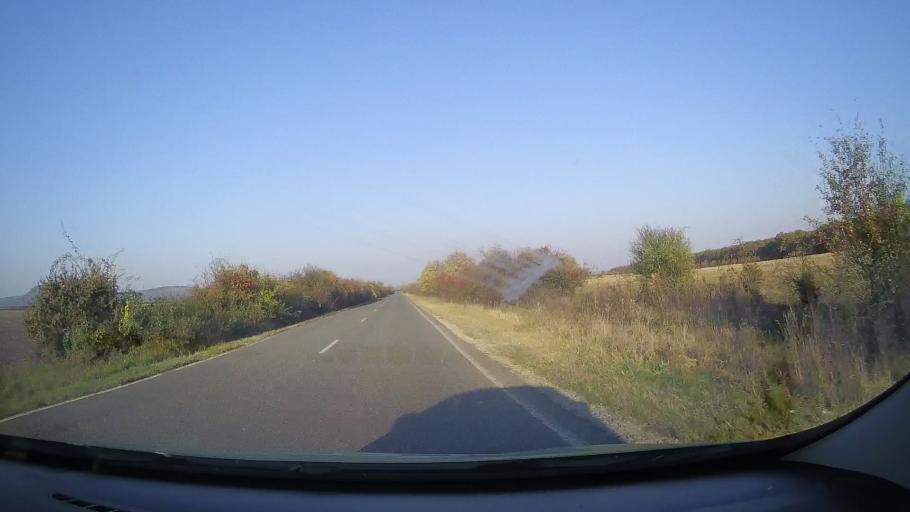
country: RO
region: Arad
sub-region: Comuna Tarnova
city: Chier
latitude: 46.3248
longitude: 21.8322
